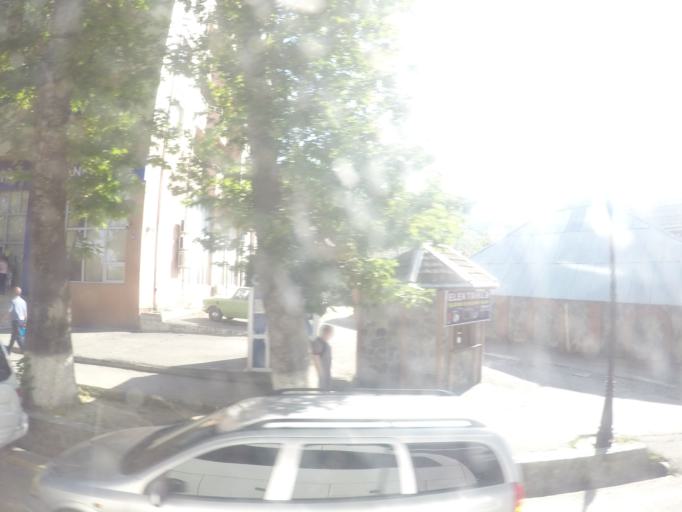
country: AZ
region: Shaki City
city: Sheki
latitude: 41.2057
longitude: 47.1777
